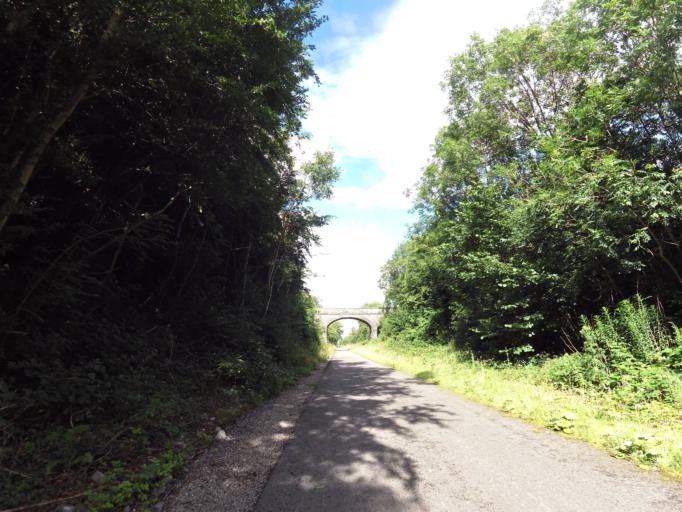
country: IE
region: Leinster
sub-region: An Iarmhi
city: Kilbeggan
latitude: 53.4403
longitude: -7.5559
